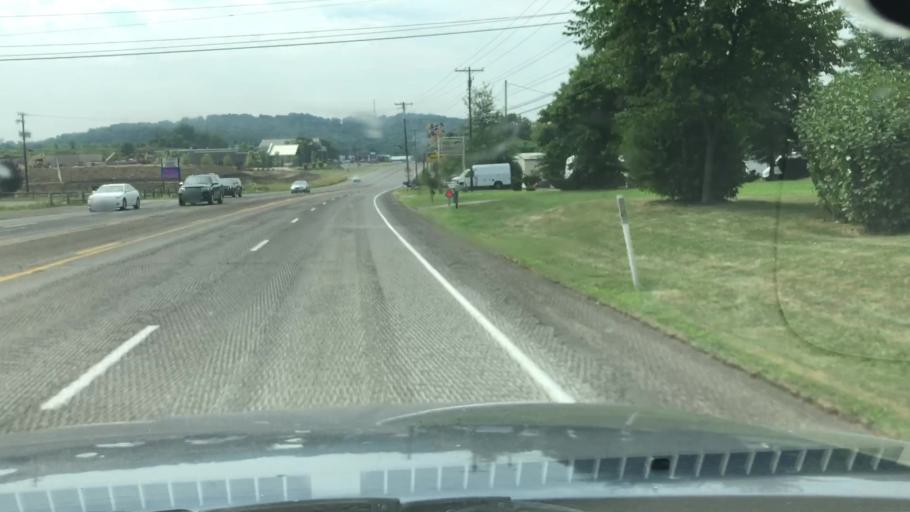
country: US
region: Pennsylvania
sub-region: Butler County
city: Nixon
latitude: 40.7650
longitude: -79.9249
